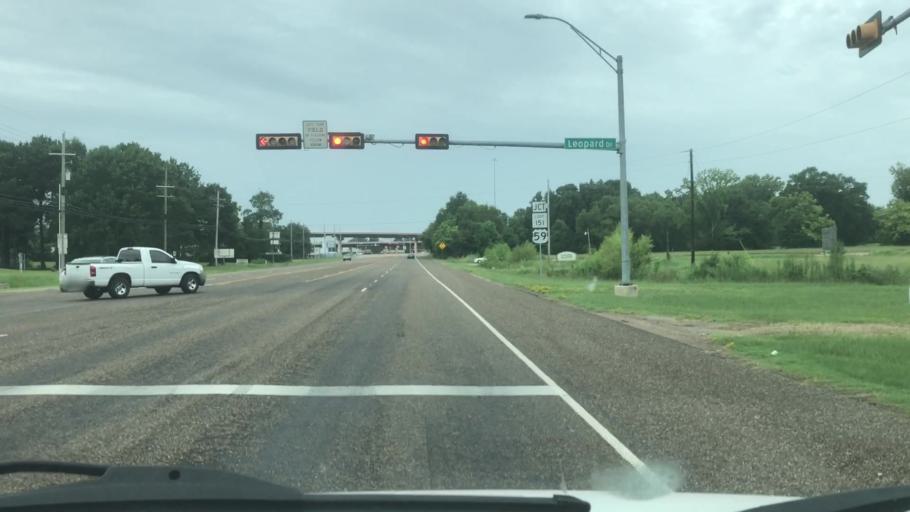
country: US
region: Texas
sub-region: Bowie County
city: Wake Village
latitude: 33.3968
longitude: -94.0920
